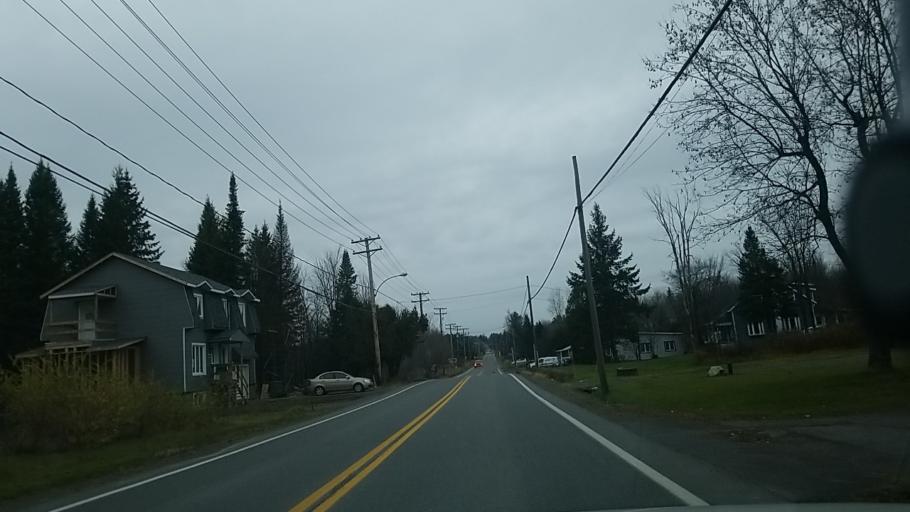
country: CA
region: Quebec
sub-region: Laurentides
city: Saint-Jerome
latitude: 45.7801
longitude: -74.0511
